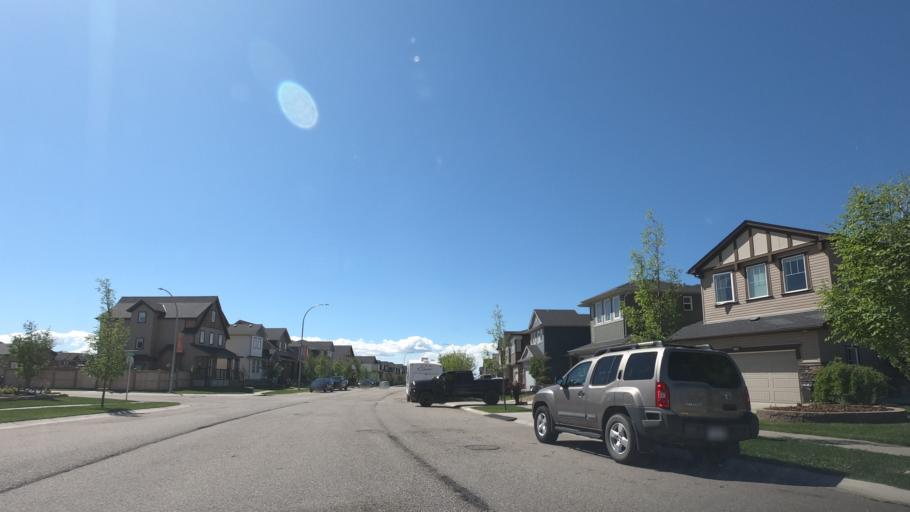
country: CA
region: Alberta
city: Airdrie
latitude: 51.2659
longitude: -113.9749
